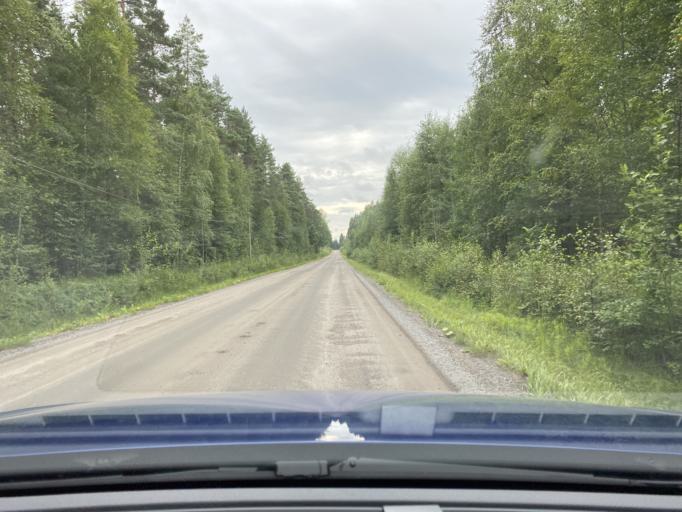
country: FI
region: Satakunta
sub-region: Rauma
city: Kiukainen
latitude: 61.1415
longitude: 21.9953
